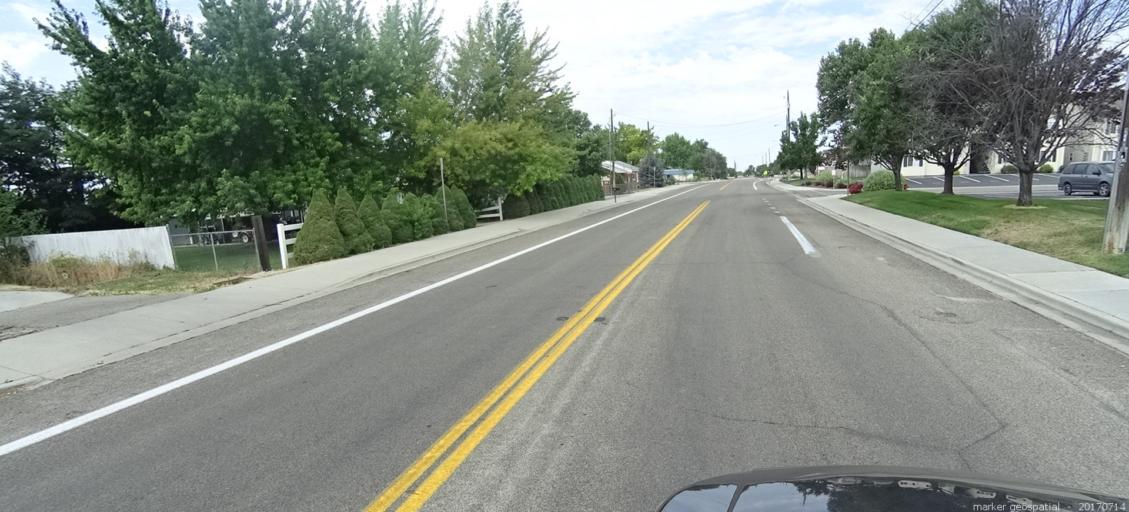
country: US
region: Idaho
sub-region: Ada County
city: Kuna
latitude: 43.4958
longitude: -116.4148
